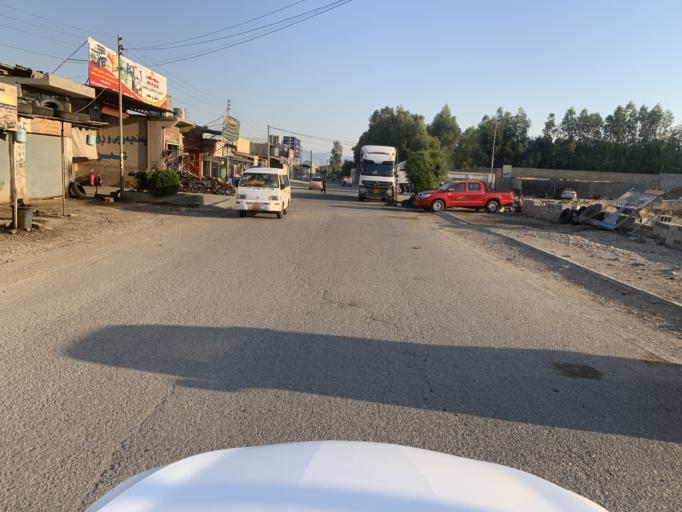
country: IQ
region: As Sulaymaniyah
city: Raniye
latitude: 36.2469
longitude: 44.8854
